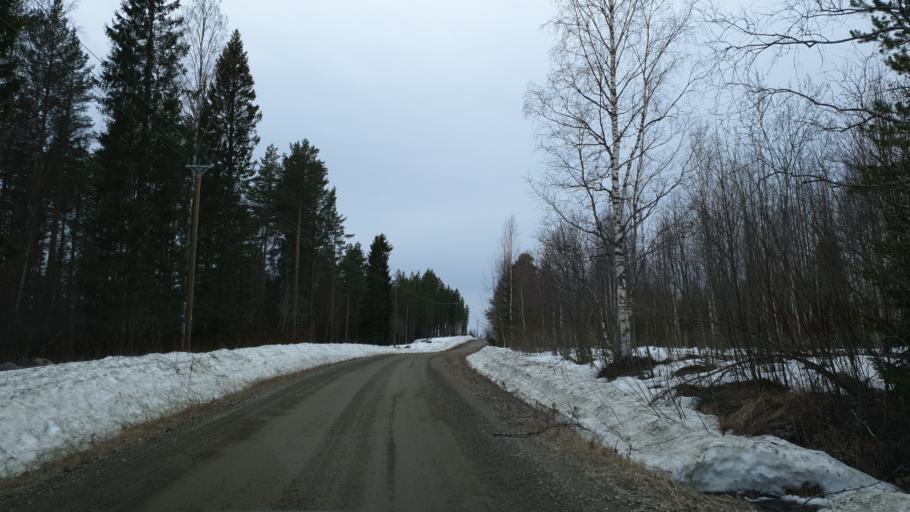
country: SE
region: Vaesterbotten
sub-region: Robertsfors Kommun
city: Robertsfors
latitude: 64.3896
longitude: 20.9662
